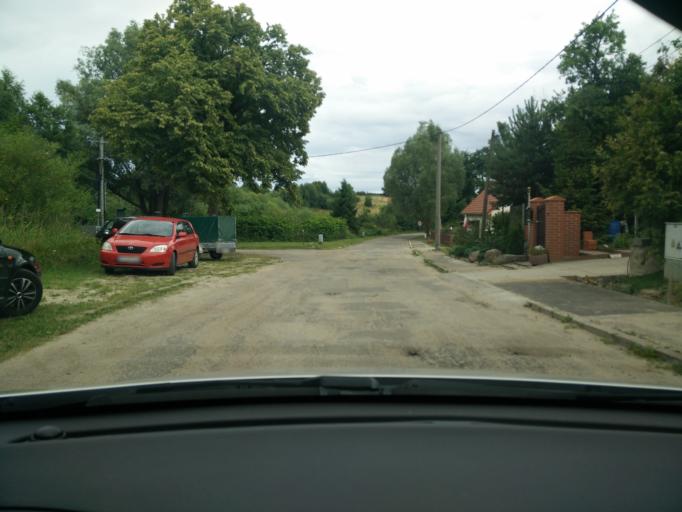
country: PL
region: Pomeranian Voivodeship
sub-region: Powiat pucki
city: Mrzezino
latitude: 54.6652
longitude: 18.4561
